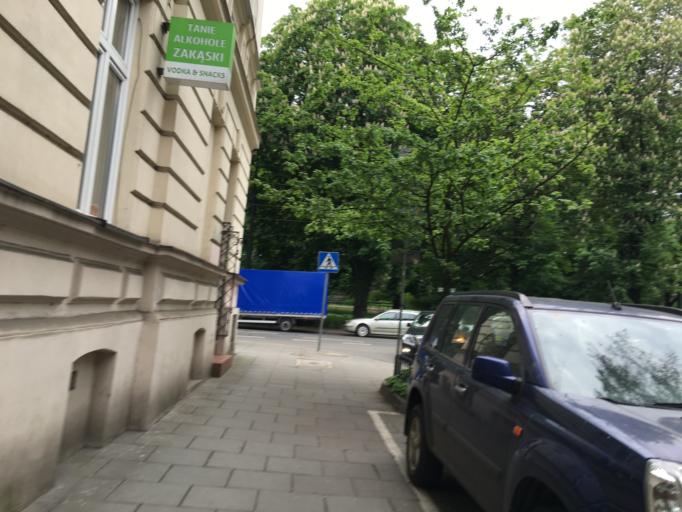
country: PL
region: Lesser Poland Voivodeship
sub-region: Krakow
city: Krakow
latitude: 50.0557
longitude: 19.9406
